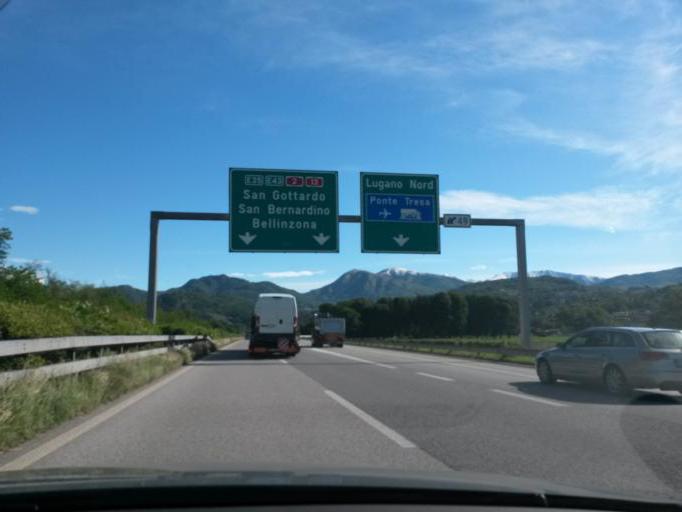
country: CH
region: Ticino
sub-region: Lugano District
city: Bioggio
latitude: 46.0223
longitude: 8.9215
